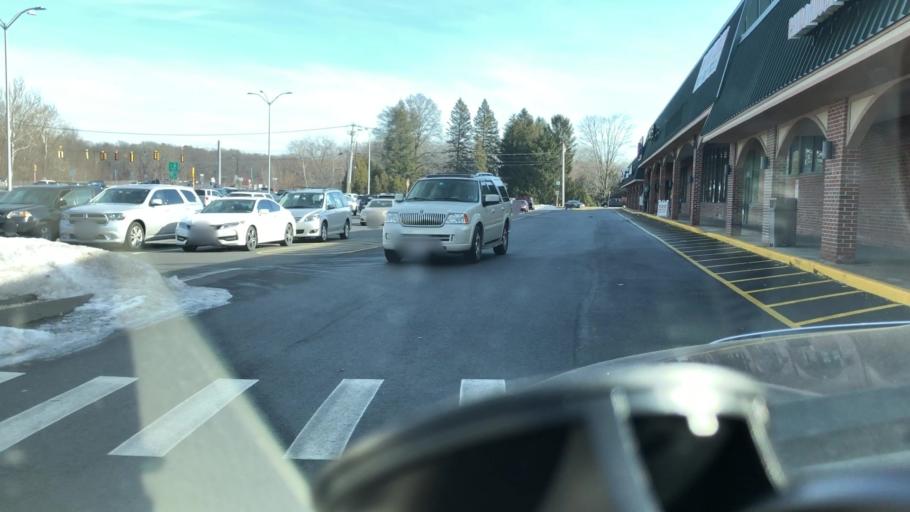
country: US
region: Massachusetts
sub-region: Hampden County
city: Westfield
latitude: 42.1121
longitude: -72.7206
